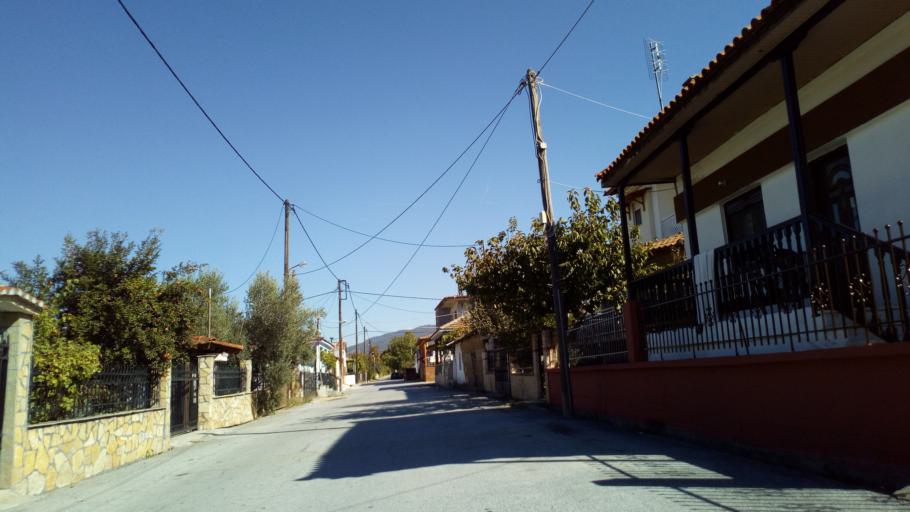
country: GR
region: Central Macedonia
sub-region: Nomos Thessalonikis
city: Gerakarou
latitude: 40.6348
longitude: 23.2471
